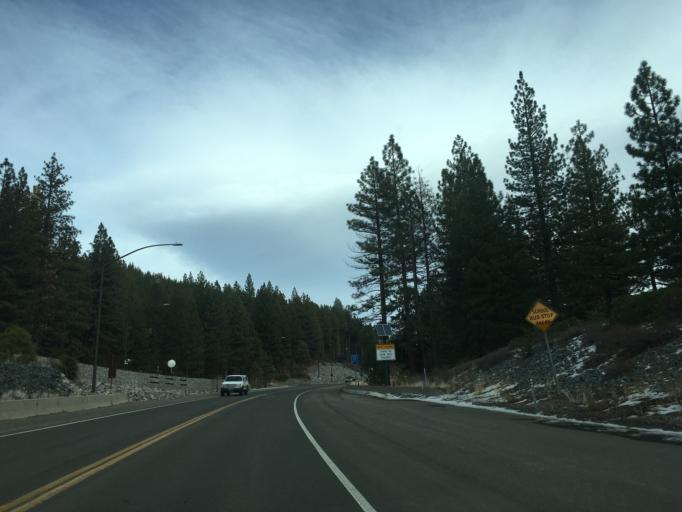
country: US
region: Nevada
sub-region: Washoe County
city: Incline Village
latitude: 39.2532
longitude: -119.9717
